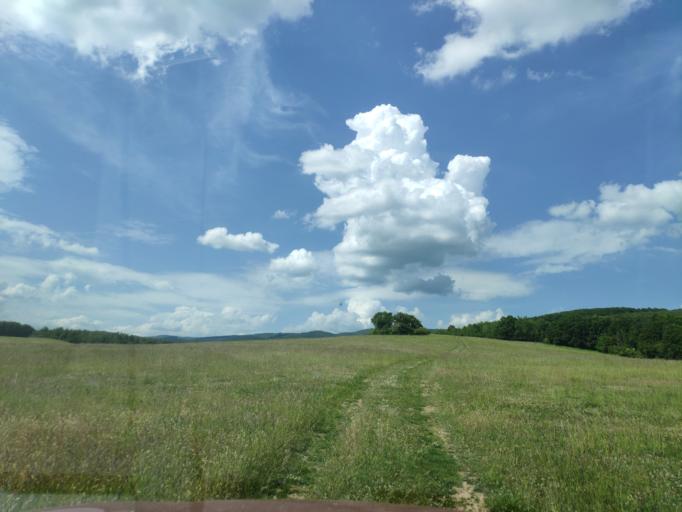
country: SK
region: Kosicky
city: Medzev
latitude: 48.7165
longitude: 20.9628
